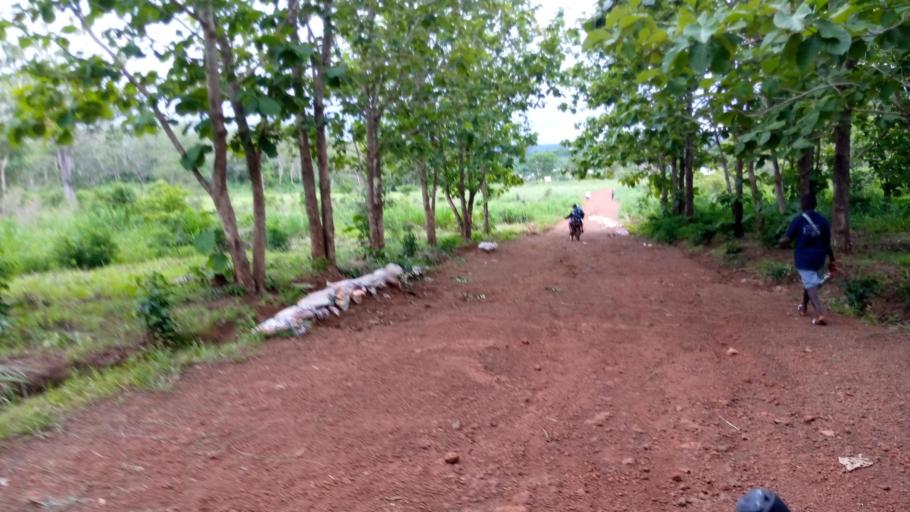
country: SL
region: Southern Province
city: Moyamba
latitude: 8.1616
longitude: -12.4530
